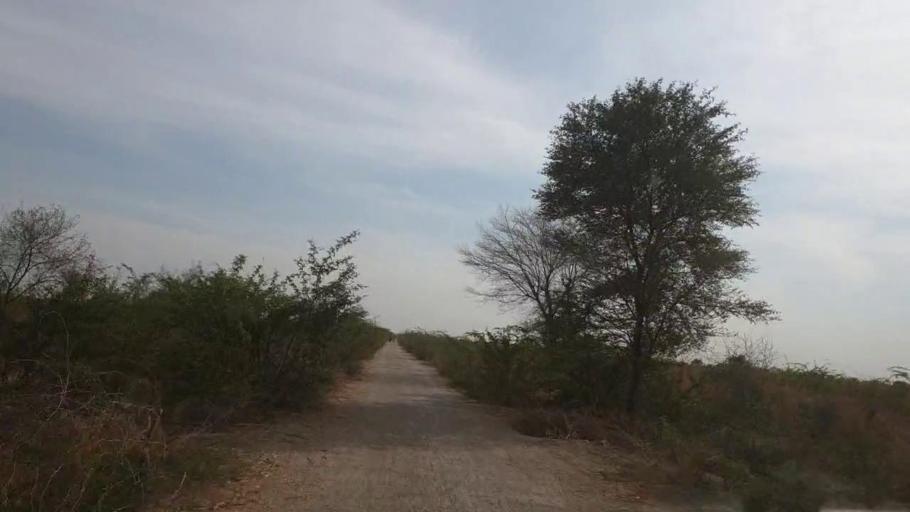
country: PK
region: Sindh
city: Nabisar
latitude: 25.0164
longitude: 69.5622
